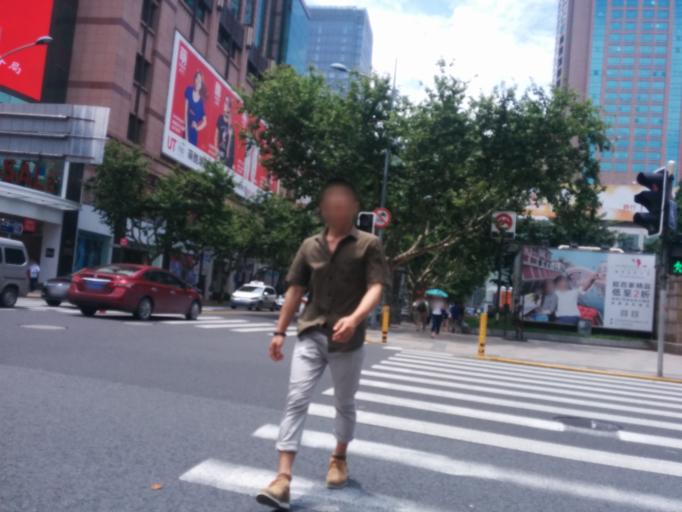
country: CN
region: Shanghai Shi
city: Shanghai
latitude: 31.2197
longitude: 121.4566
